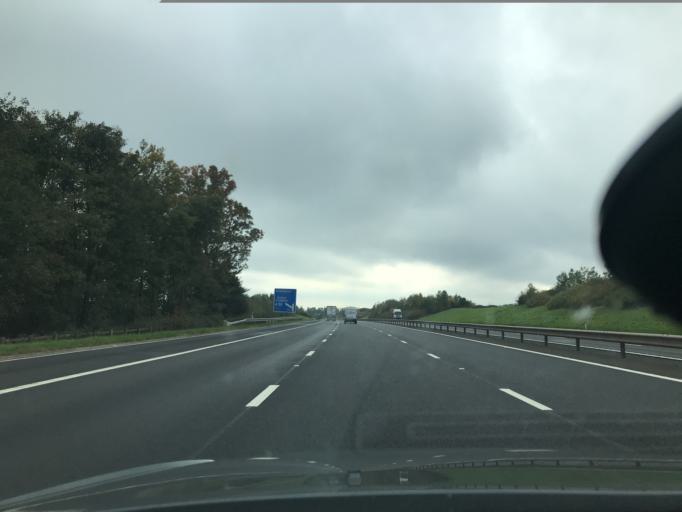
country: GB
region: England
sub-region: City and Borough of Birmingham
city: Sutton Coldfield
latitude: 52.5979
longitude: -1.7968
